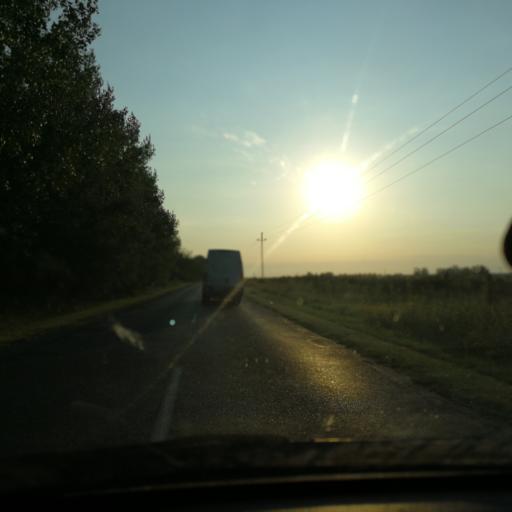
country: HU
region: Bacs-Kiskun
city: Kiskunhalas
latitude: 46.4422
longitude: 19.5854
